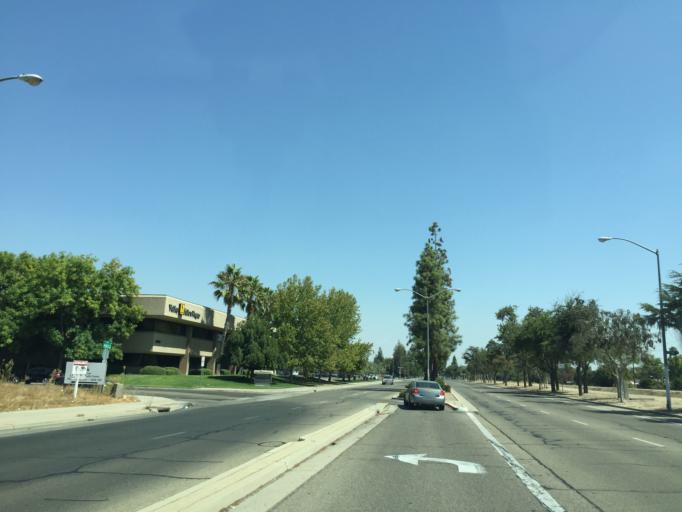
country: US
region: California
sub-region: Fresno County
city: Sunnyside
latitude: 36.7652
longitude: -119.7297
